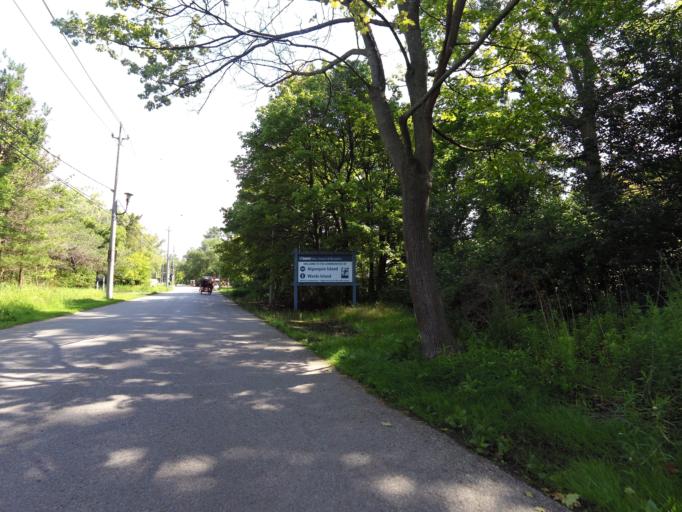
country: CA
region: Ontario
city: Toronto
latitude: 43.6267
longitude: -79.3578
